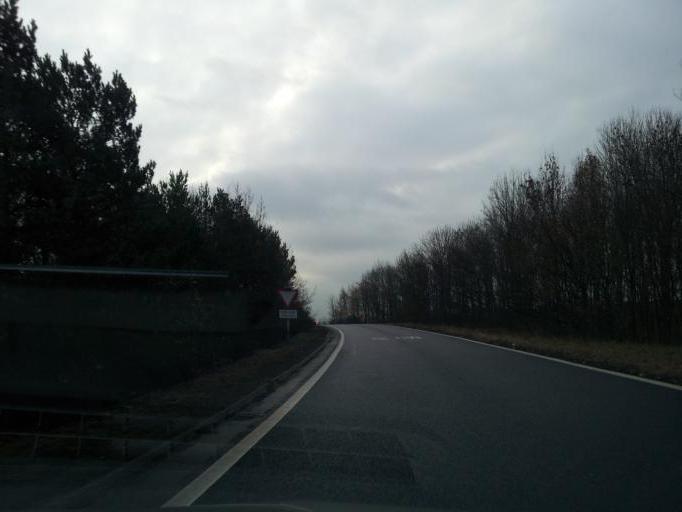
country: GB
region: England
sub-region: Cambridgeshire
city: Barton
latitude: 52.1939
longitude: 0.0748
